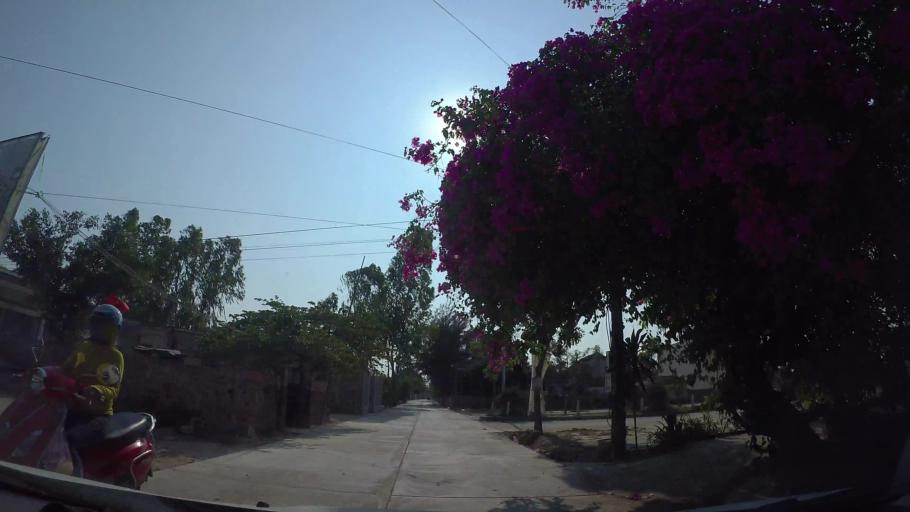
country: VN
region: Da Nang
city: Ngu Hanh Son
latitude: 15.9587
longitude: 108.2624
